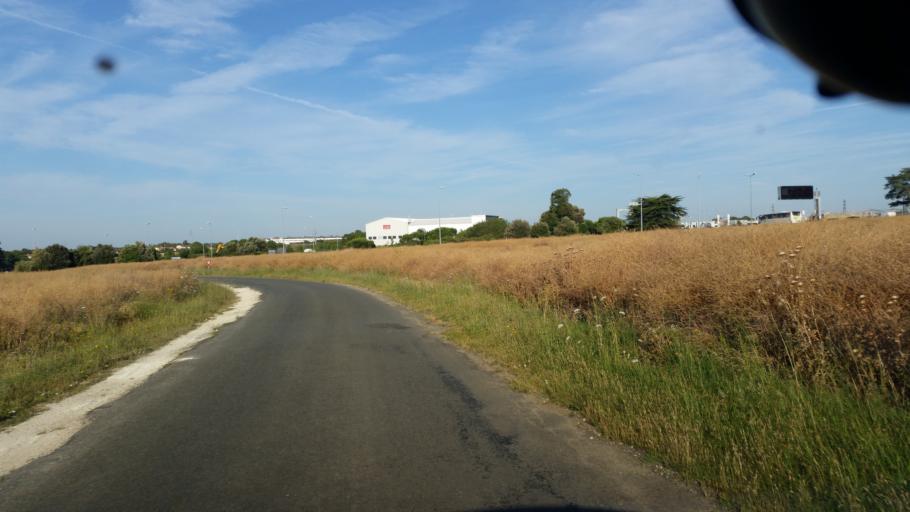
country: FR
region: Poitou-Charentes
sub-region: Departement de la Charente-Maritime
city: Puilboreau
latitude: 46.1743
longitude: -1.1097
